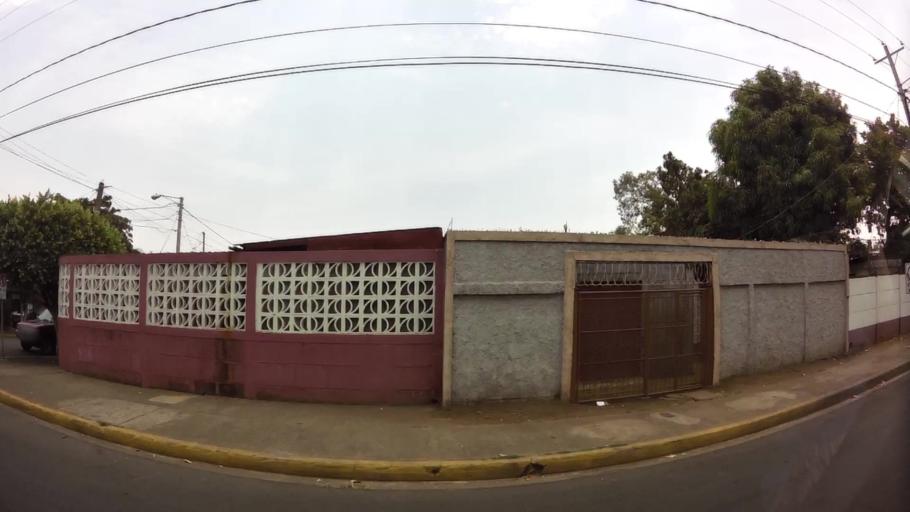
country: NI
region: Managua
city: Managua
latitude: 12.1321
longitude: -86.2948
